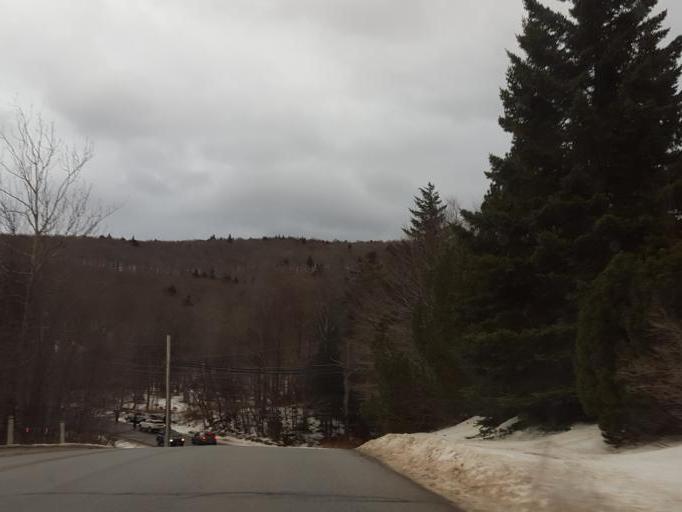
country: US
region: Vermont
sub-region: Rutland County
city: Rutland
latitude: 43.6259
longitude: -72.7895
